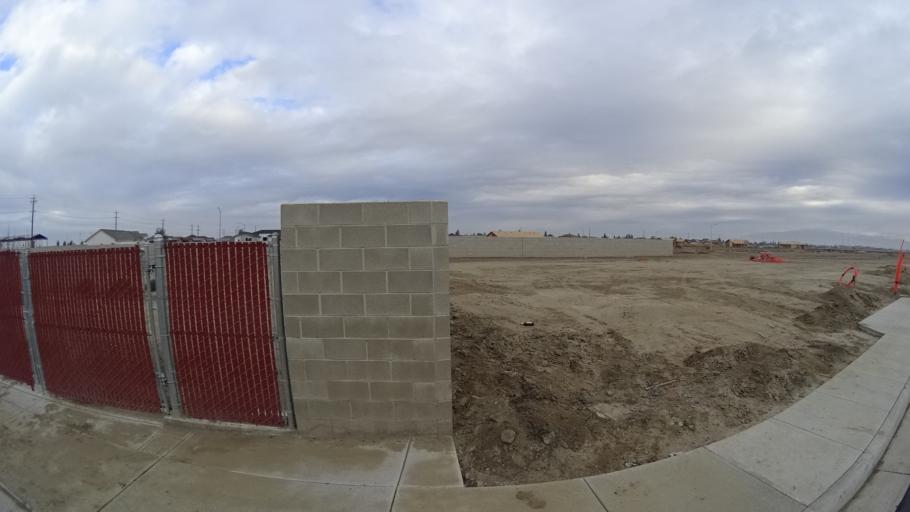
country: US
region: California
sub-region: Kern County
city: Greenfield
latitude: 35.2918
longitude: -119.0912
